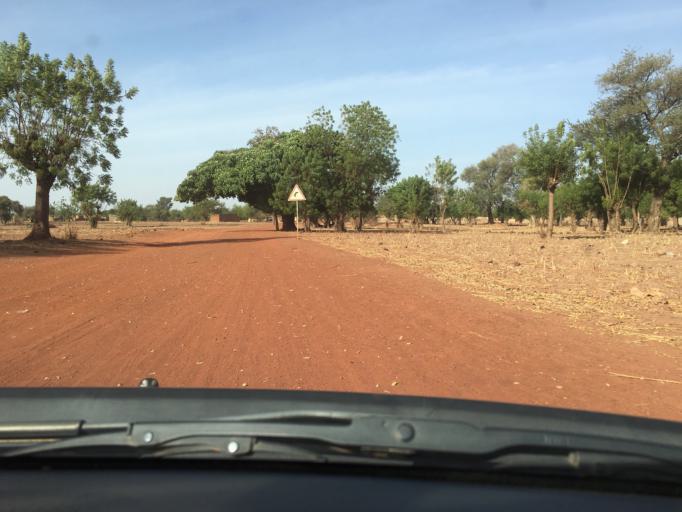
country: BF
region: Plateau-Central
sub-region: Province du Kourweogo
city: Bousse
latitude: 12.5667
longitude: -1.9218
